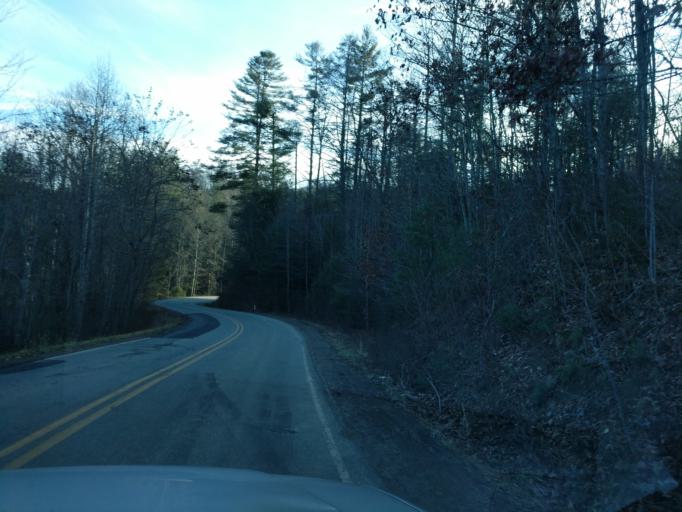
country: US
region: North Carolina
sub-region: Haywood County
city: Cove Creek
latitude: 35.6673
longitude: -83.0148
